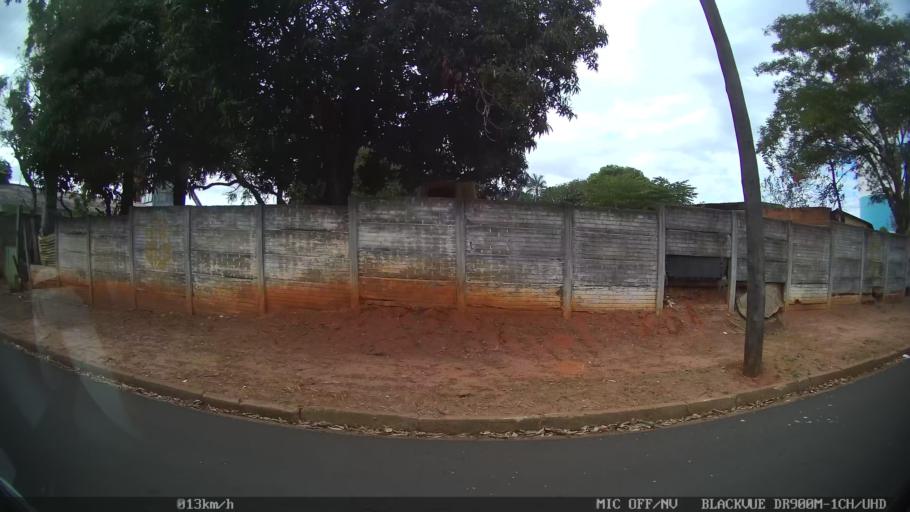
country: BR
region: Sao Paulo
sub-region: Bady Bassitt
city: Bady Bassitt
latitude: -20.8137
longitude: -49.4973
